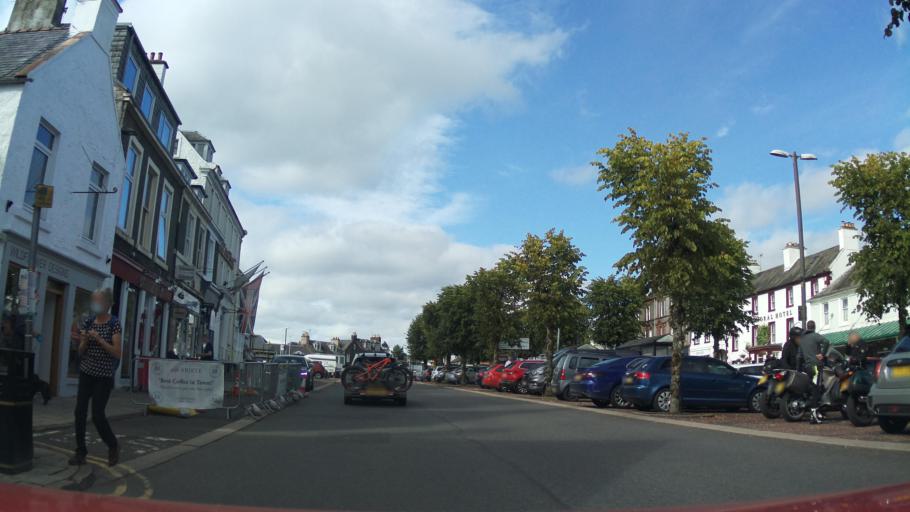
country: GB
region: Scotland
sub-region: Dumfries and Galloway
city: Moffat
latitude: 55.3329
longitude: -3.4442
